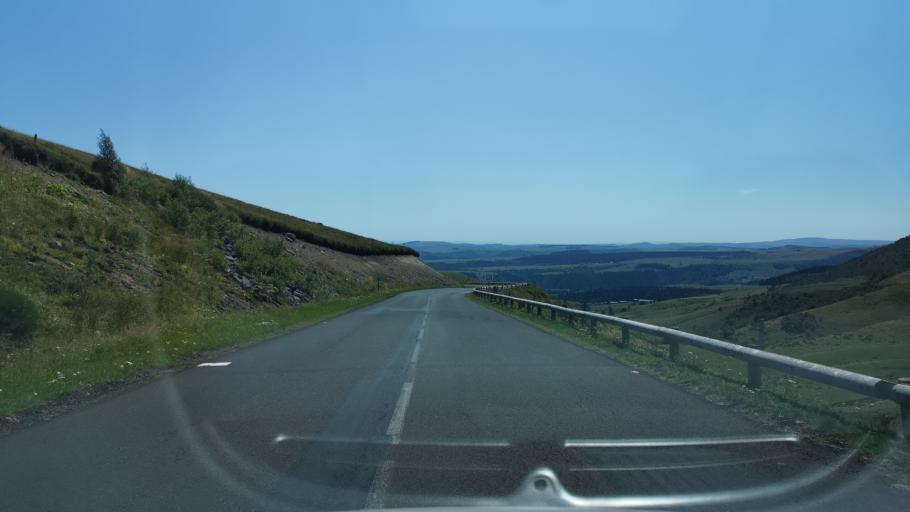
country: FR
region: Auvergne
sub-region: Departement du Puy-de-Dome
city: Mont-Dore
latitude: 45.5952
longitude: 2.8522
